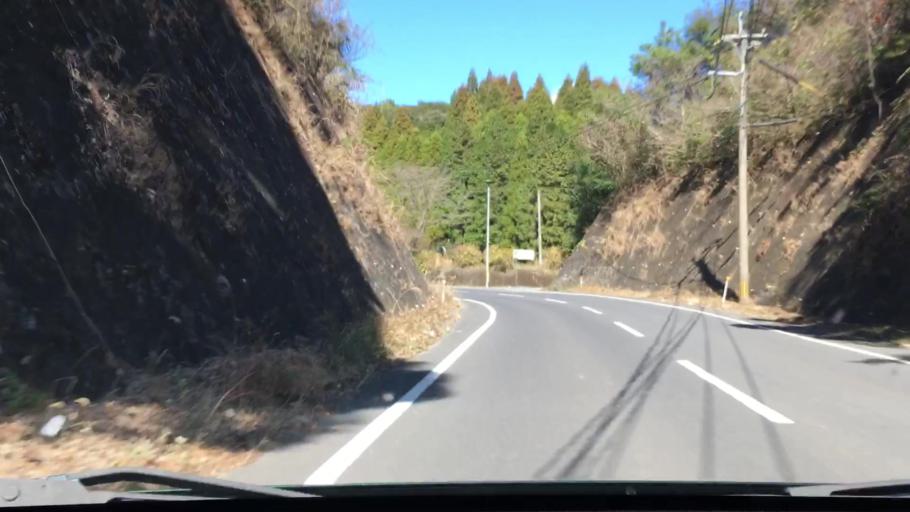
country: JP
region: Kagoshima
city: Ijuin
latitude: 31.7015
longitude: 130.4550
